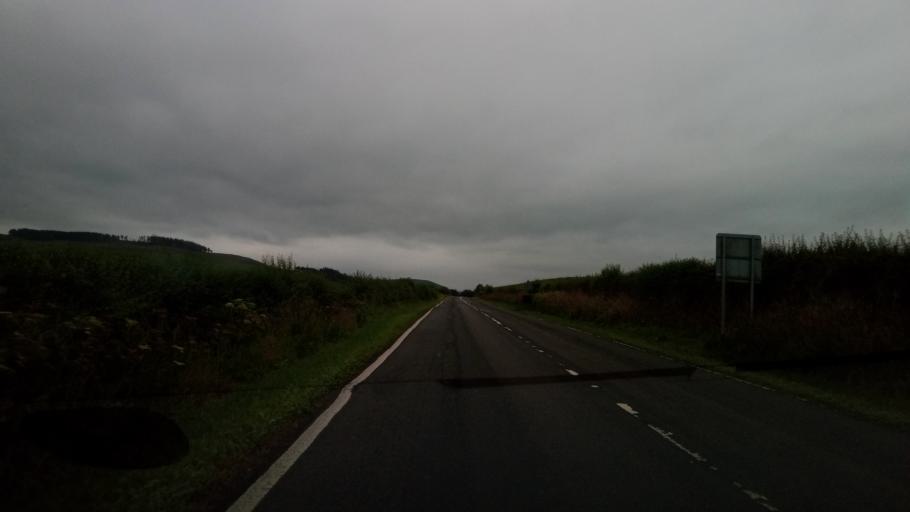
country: GB
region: Scotland
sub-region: The Scottish Borders
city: Hawick
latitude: 55.3741
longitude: -2.8764
